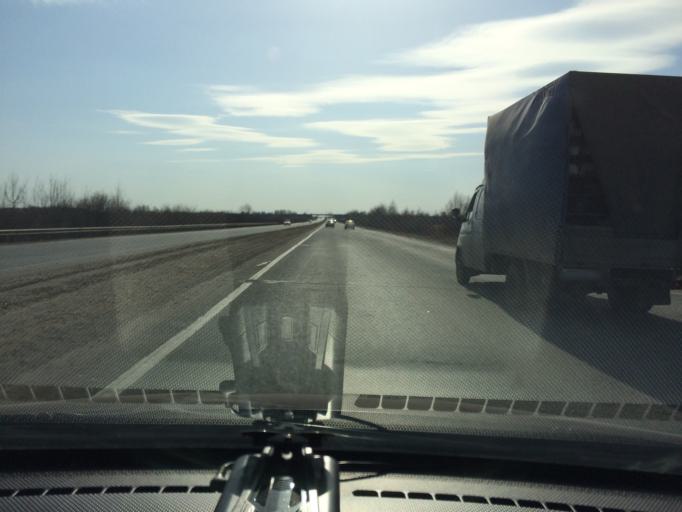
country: RU
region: Mariy-El
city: Yoshkar-Ola
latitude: 56.6857
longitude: 48.0384
